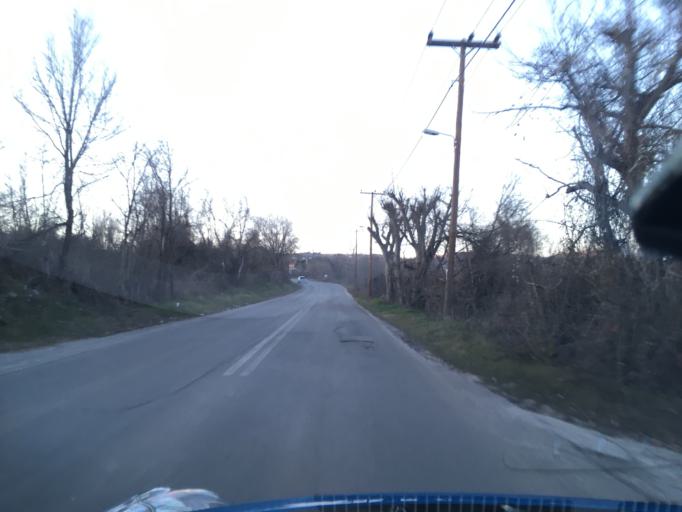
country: GR
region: West Macedonia
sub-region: Nomos Kozanis
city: Kozani
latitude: 40.2829
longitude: 21.7815
